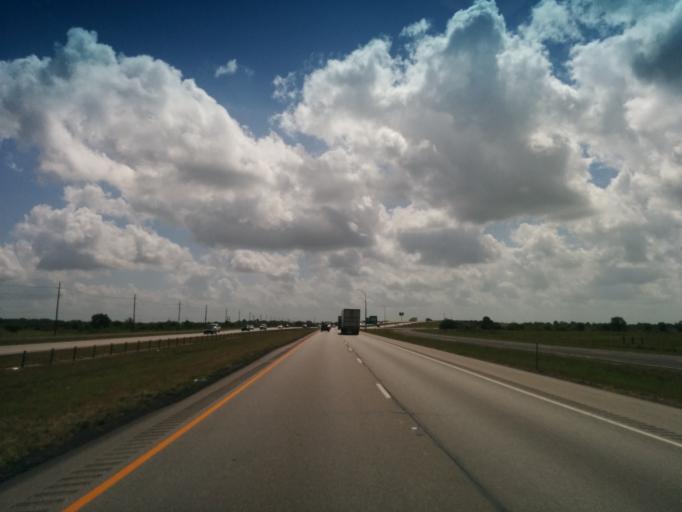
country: US
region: Texas
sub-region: Austin County
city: Sealy
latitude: 29.7632
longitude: -96.1941
